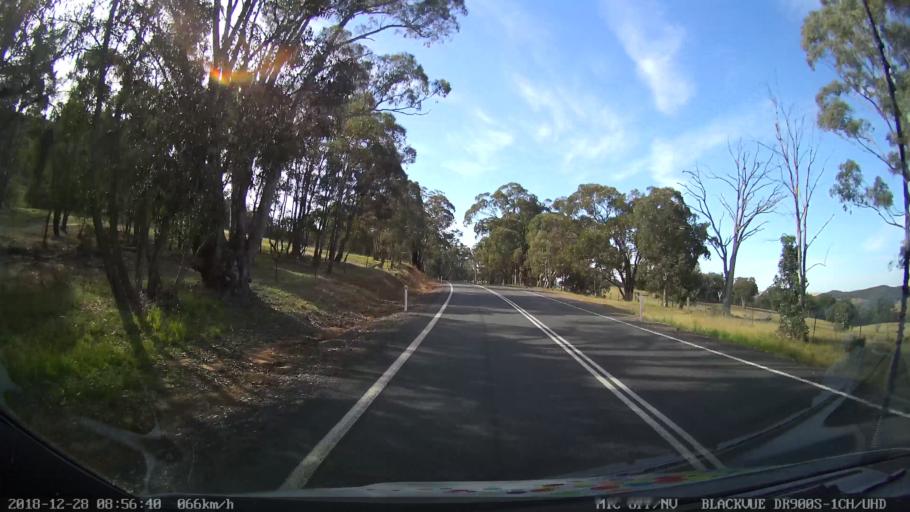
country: AU
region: New South Wales
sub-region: Upper Lachlan Shire
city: Crookwell
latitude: -34.1123
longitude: 149.3378
